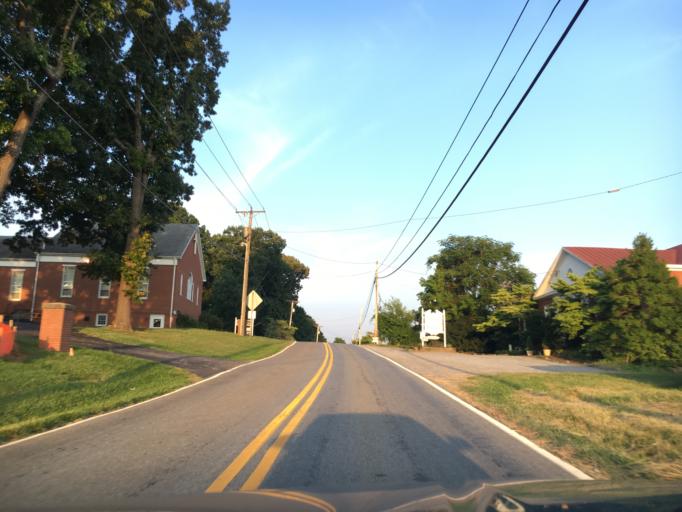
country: US
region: Virginia
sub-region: Bedford County
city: Forest
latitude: 37.3633
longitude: -79.2896
